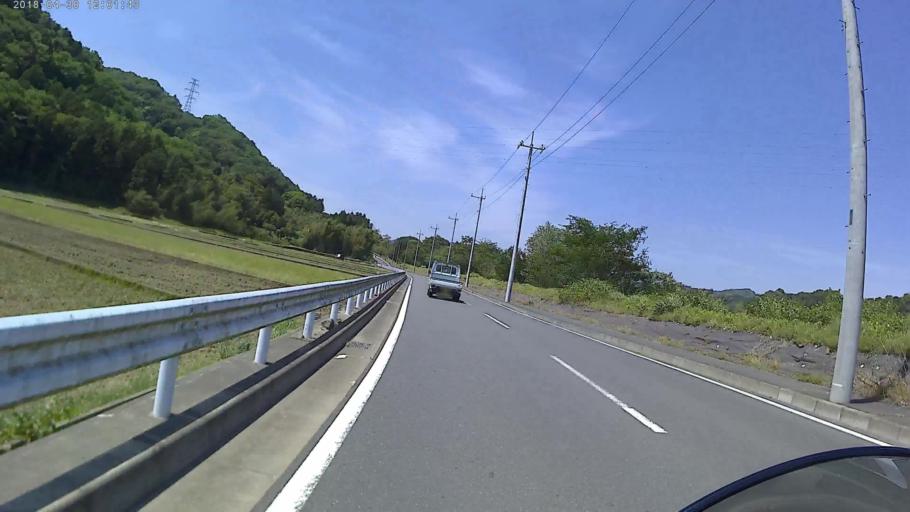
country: JP
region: Kanagawa
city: Zama
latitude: 35.5193
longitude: 139.3240
